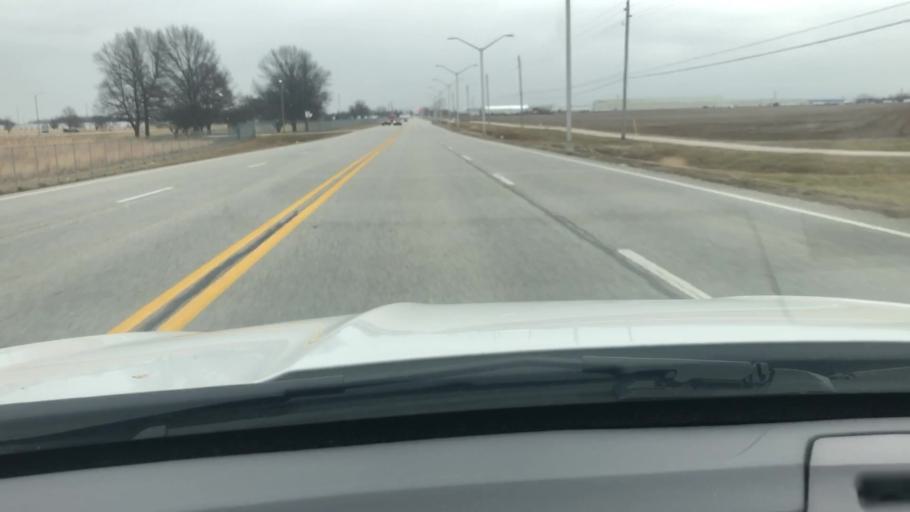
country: US
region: Indiana
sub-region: Tippecanoe County
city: Lafayette
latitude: 40.3673
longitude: -86.8500
